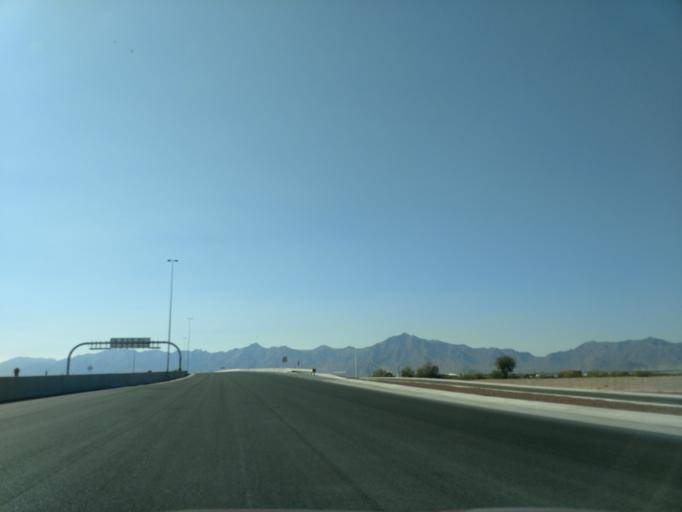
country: US
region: Arizona
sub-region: Maricopa County
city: Laveen
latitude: 33.3670
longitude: -112.1912
